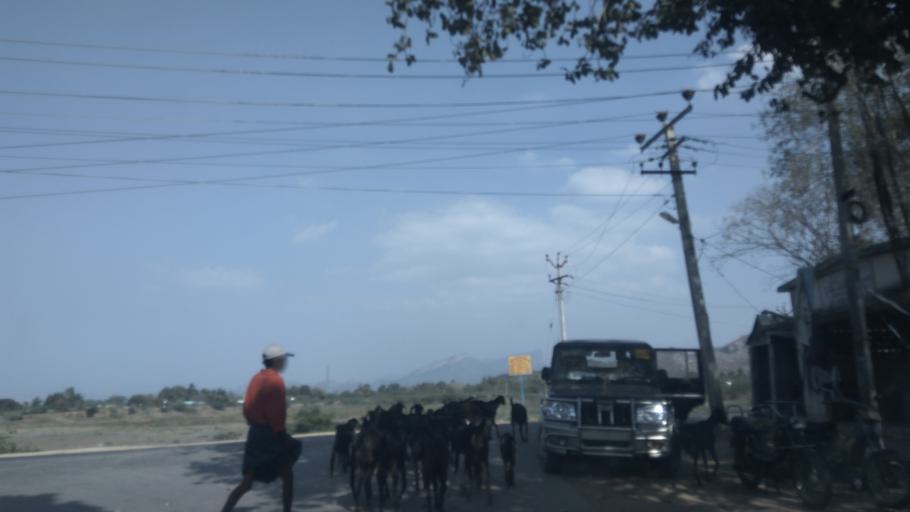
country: IN
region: Andhra Pradesh
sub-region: Chittoor
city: Renigunta
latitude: 13.5373
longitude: 79.4792
